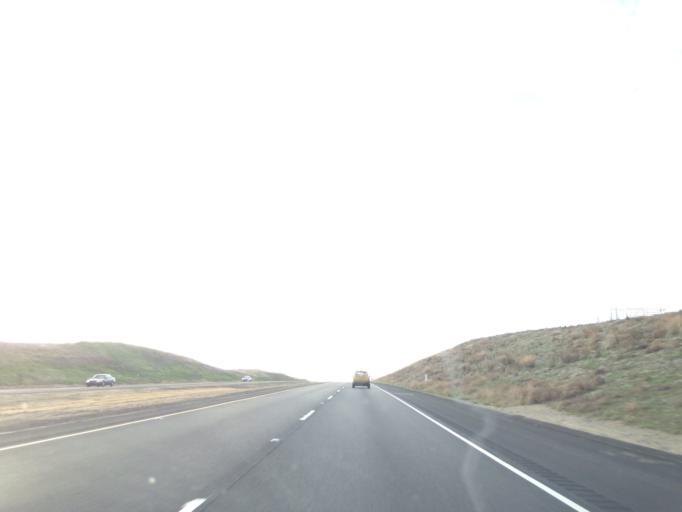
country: US
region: California
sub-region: San Luis Obispo County
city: Shandon
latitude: 35.6594
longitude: -120.4746
